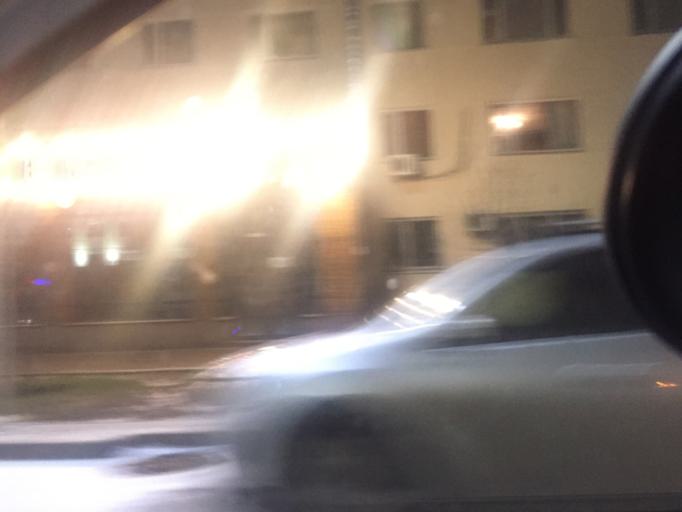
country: KZ
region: Astana Qalasy
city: Astana
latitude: 51.1849
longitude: 71.4162
